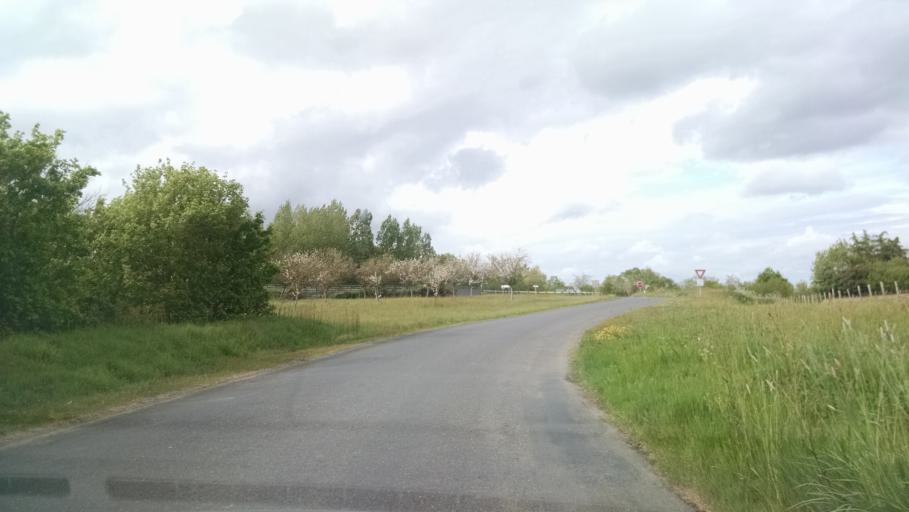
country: FR
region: Pays de la Loire
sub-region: Departement de la Vendee
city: Saint-Hilaire-de-Loulay
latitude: 46.9908
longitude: -1.3504
